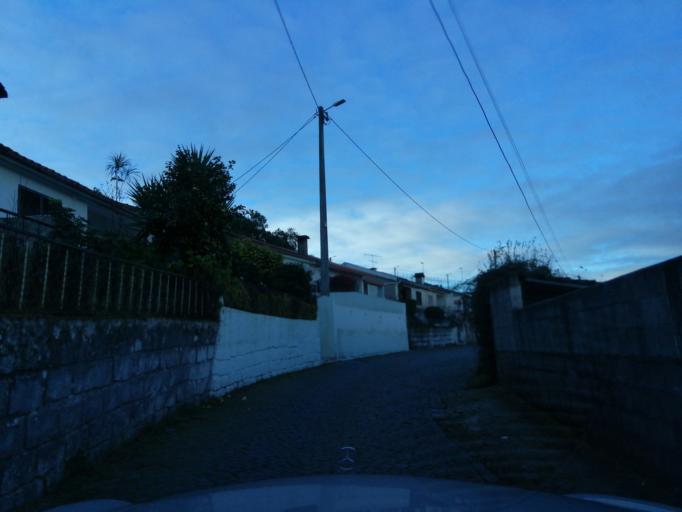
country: PT
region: Braga
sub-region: Braga
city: Braga
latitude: 41.5375
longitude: -8.4171
